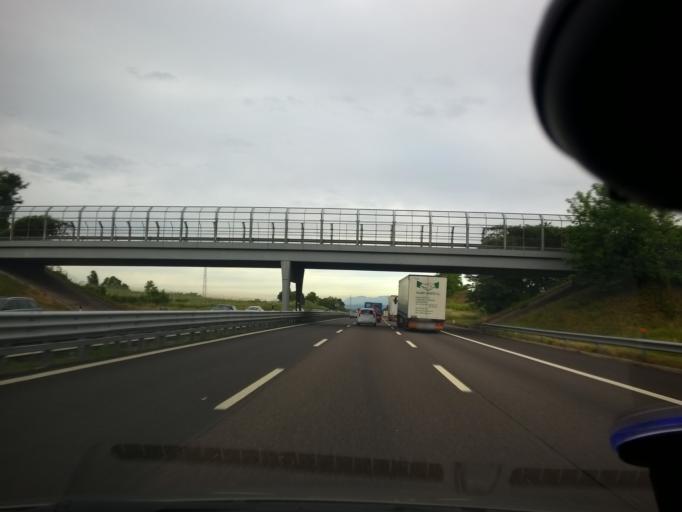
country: IT
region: Veneto
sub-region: Provincia di Verona
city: San Giorgio in Salici
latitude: 45.4220
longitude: 10.7803
